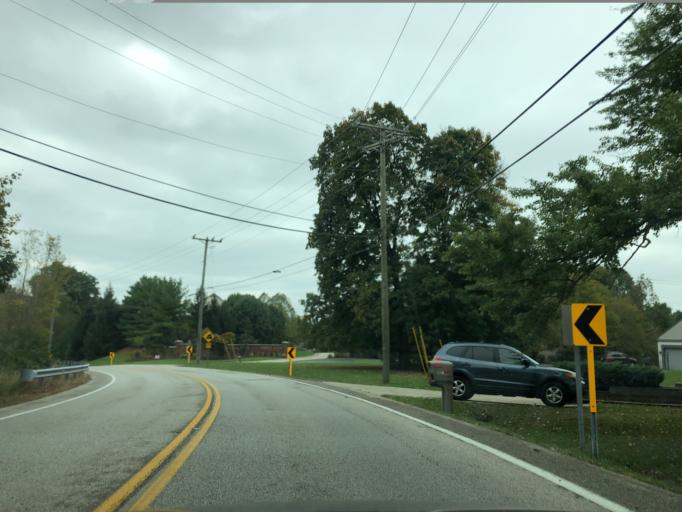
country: US
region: Ohio
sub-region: Hamilton County
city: The Village of Indian Hill
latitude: 39.2601
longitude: -84.3077
